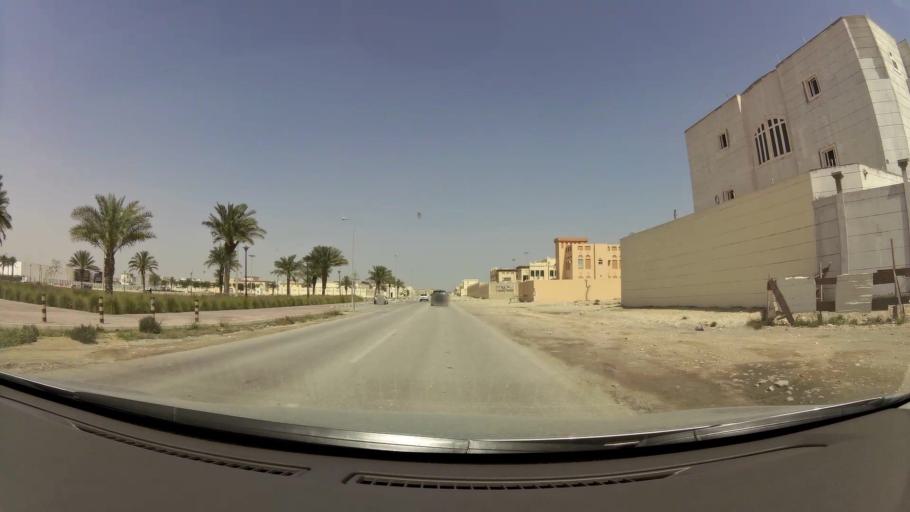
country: QA
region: Baladiyat Umm Salal
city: Umm Salal Muhammad
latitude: 25.3775
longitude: 51.4633
